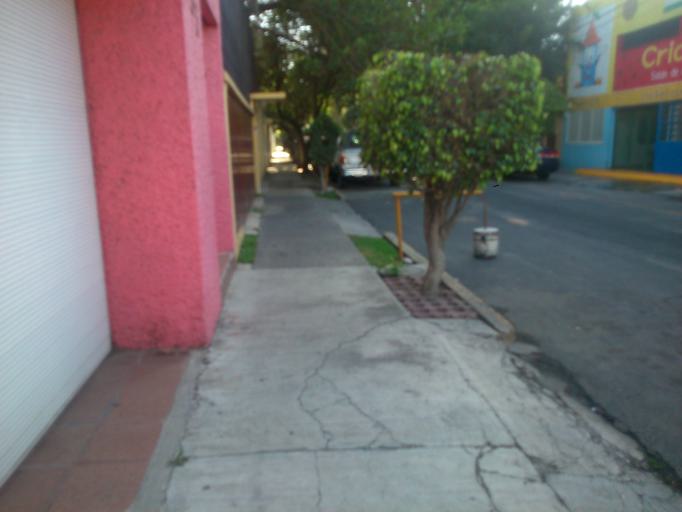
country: MX
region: Mexico
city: Colonia Lindavista
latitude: 19.4956
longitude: -99.1266
